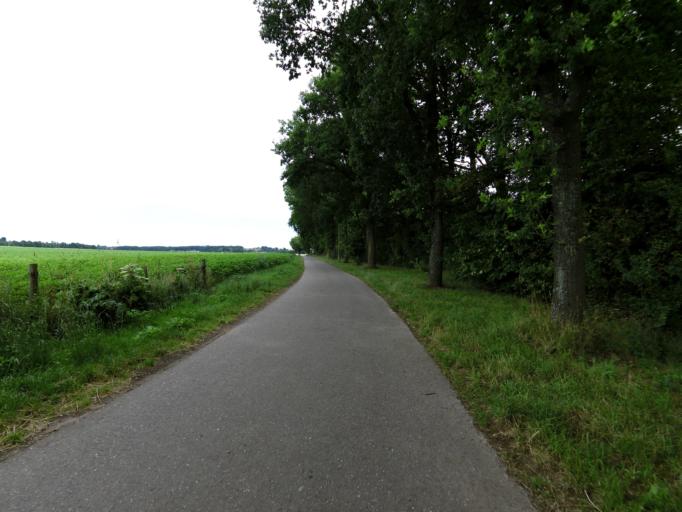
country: NL
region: Limburg
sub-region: Gemeente Schinnen
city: Amstenrade
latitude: 50.9384
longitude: 5.9167
